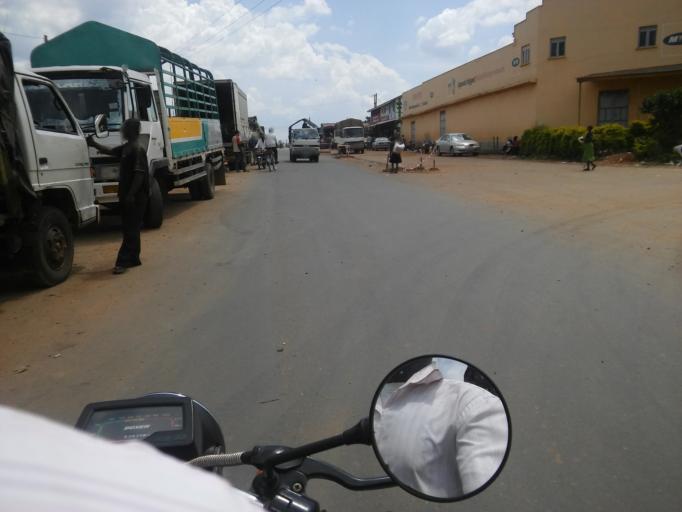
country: UG
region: Eastern Region
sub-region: Mbale District
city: Mbale
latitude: 1.0756
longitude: 34.1622
